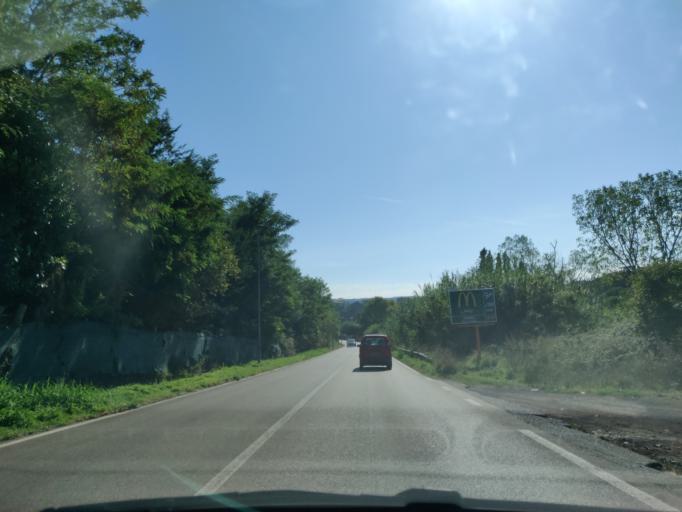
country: IT
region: Latium
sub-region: Provincia di Viterbo
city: Viterbo
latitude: 42.4157
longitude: 12.0925
